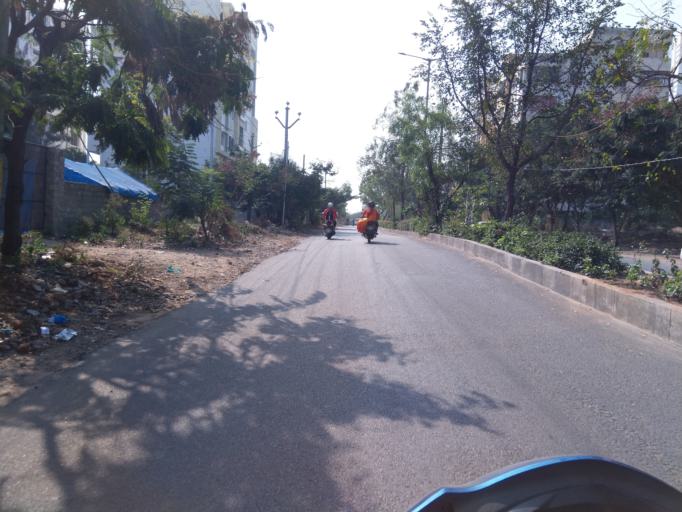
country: IN
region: Telangana
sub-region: Rangareddi
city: Kukatpalli
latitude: 17.4784
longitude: 78.3948
